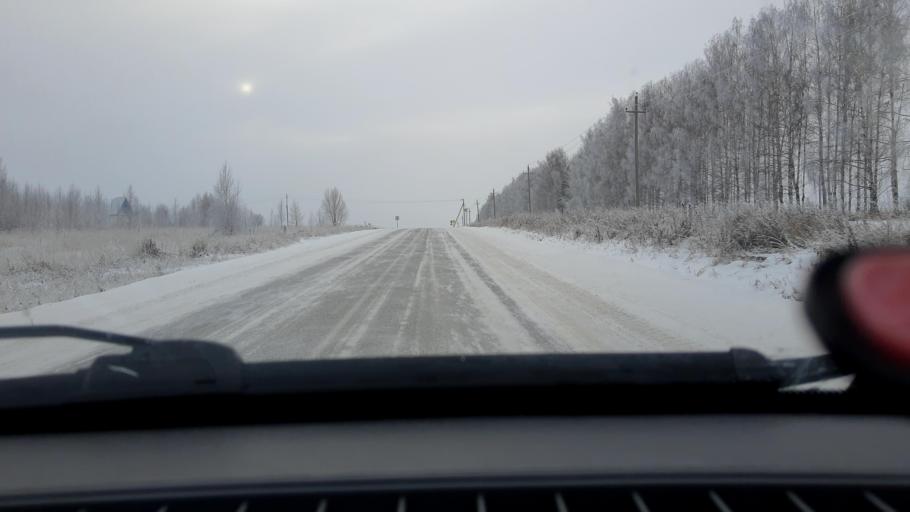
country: RU
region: Bashkortostan
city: Iglino
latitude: 54.6596
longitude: 56.4242
